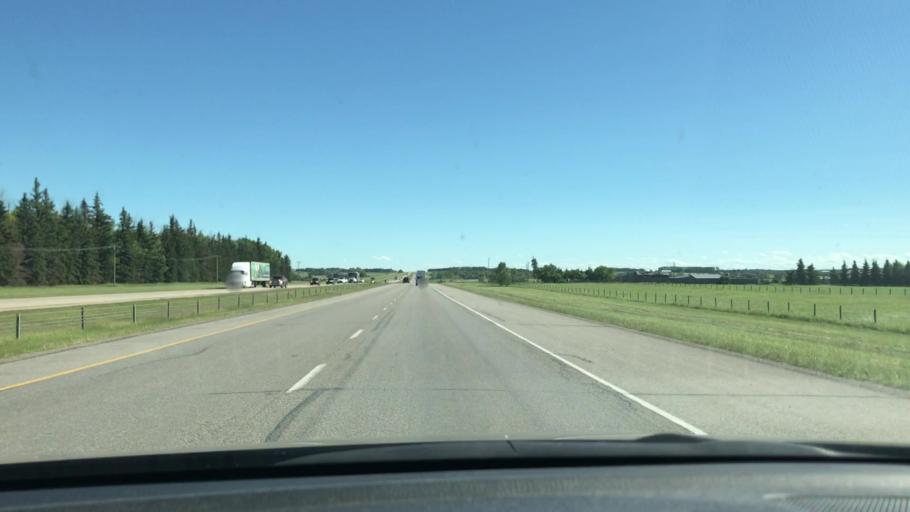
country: CA
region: Alberta
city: Olds
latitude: 51.9175
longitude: -114.0256
